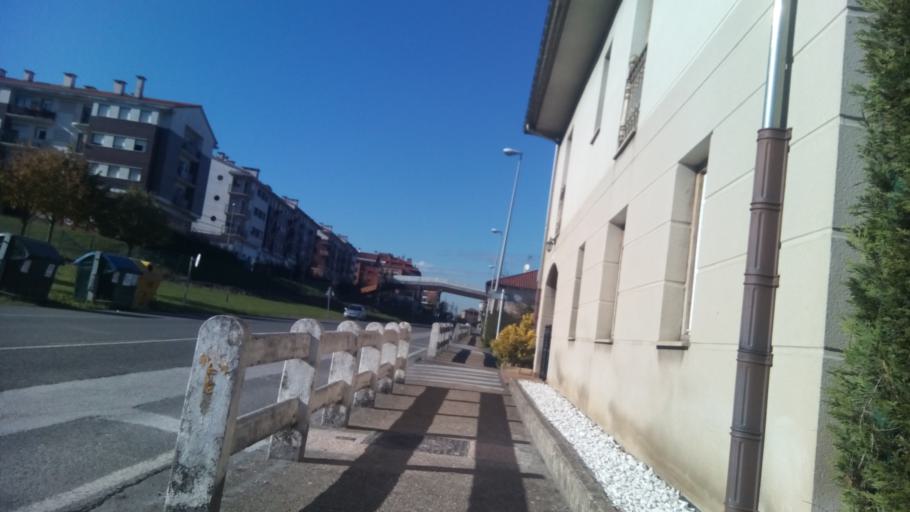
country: ES
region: Basque Country
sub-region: Bizkaia
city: Zamudio
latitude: 43.2824
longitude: -2.8590
